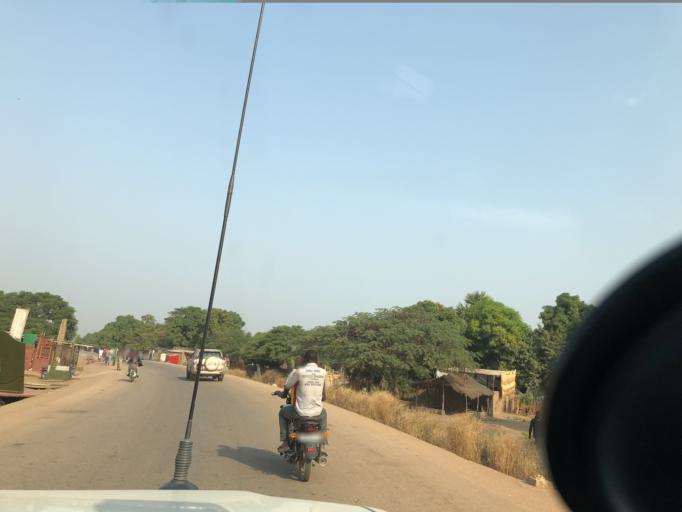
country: TD
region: Logone Occidental
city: Moundou
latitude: 8.5655
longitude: 16.0533
